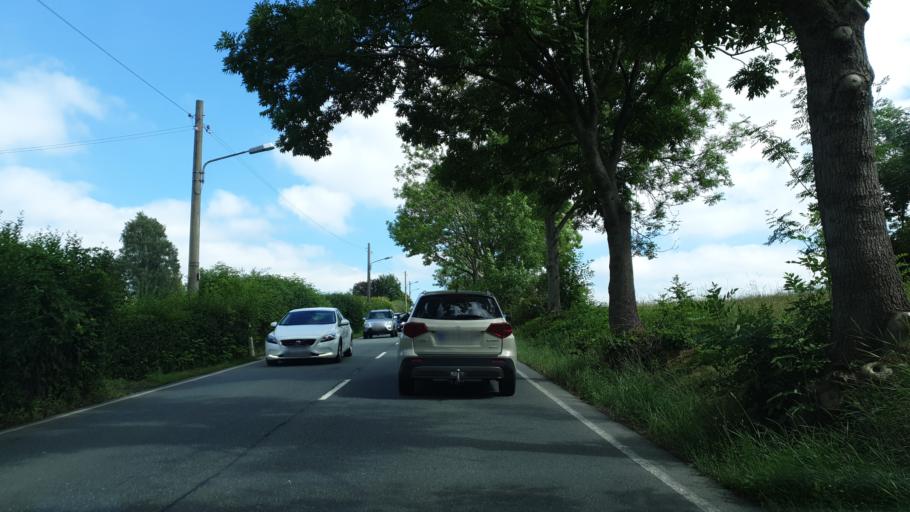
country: DE
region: Saxony
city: Neukirchen
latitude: 50.7943
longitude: 12.8666
